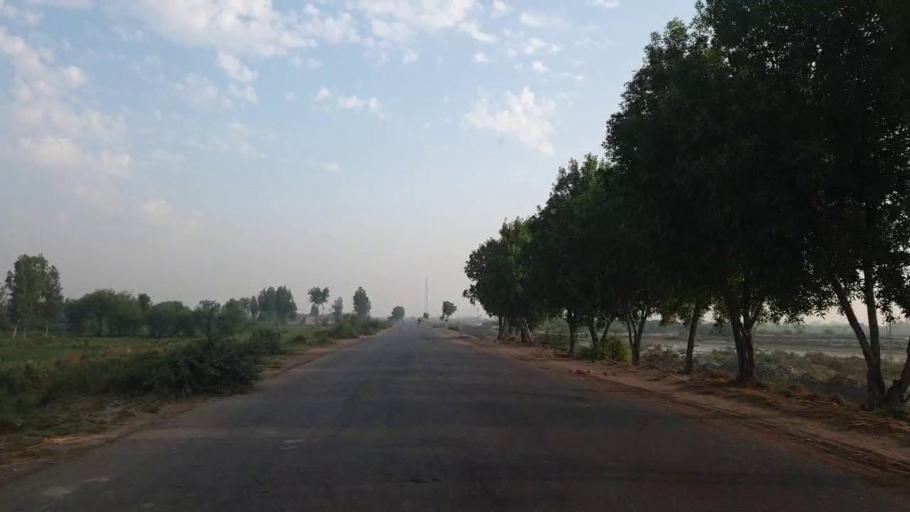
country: PK
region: Sindh
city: Badin
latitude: 24.6915
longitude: 68.9169
